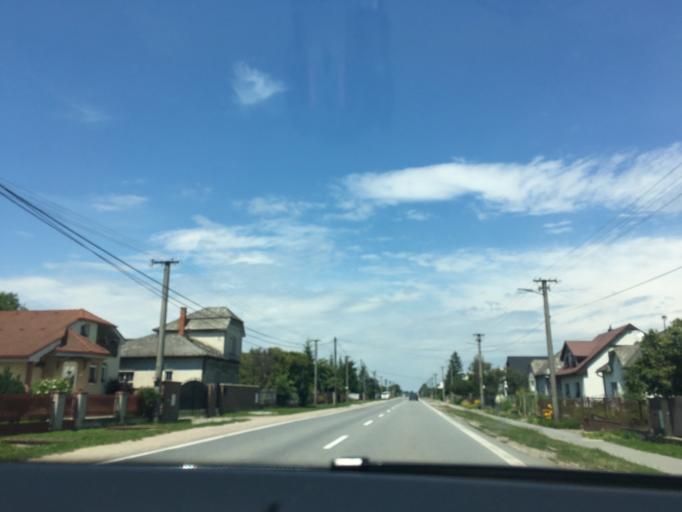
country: SK
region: Kosicky
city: Secovce
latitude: 48.7907
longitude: 21.6813
